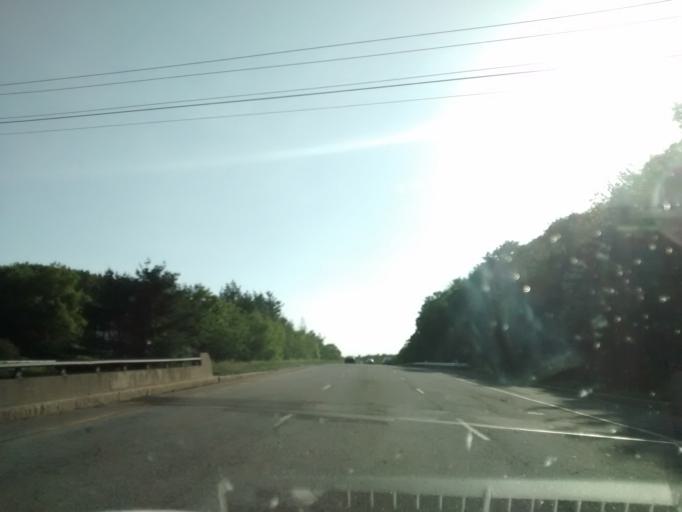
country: US
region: Massachusetts
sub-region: Worcester County
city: Northborough
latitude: 42.3424
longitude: -71.6420
